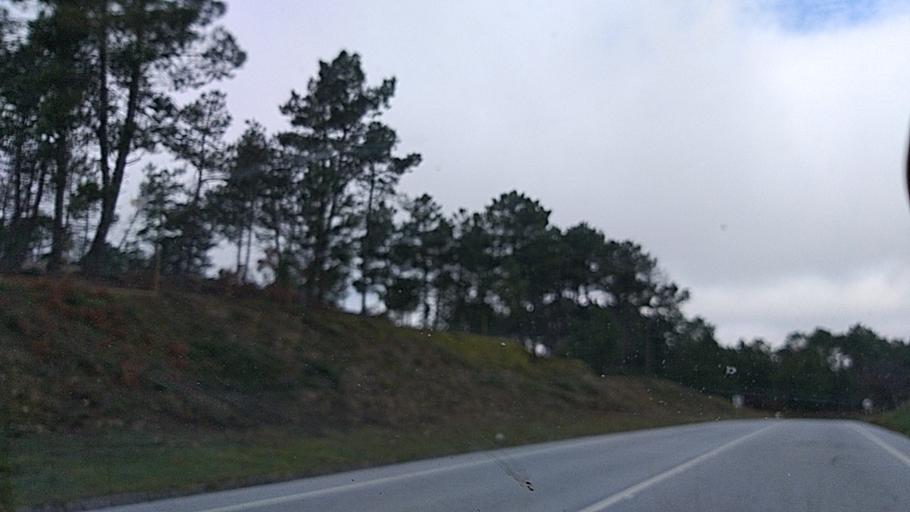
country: PT
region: Guarda
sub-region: Aguiar da Beira
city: Aguiar da Beira
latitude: 40.7438
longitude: -7.4991
